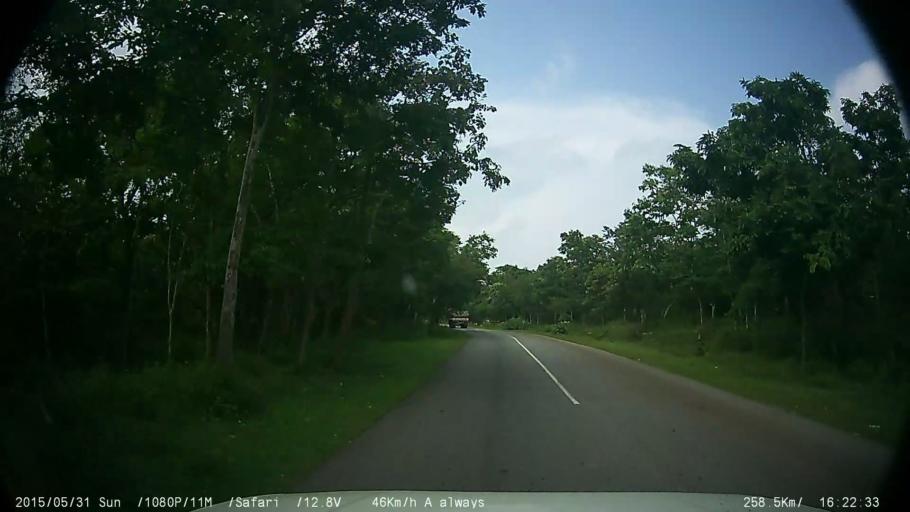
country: IN
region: Karnataka
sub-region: Chamrajnagar
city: Gundlupet
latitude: 11.7549
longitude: 76.5112
